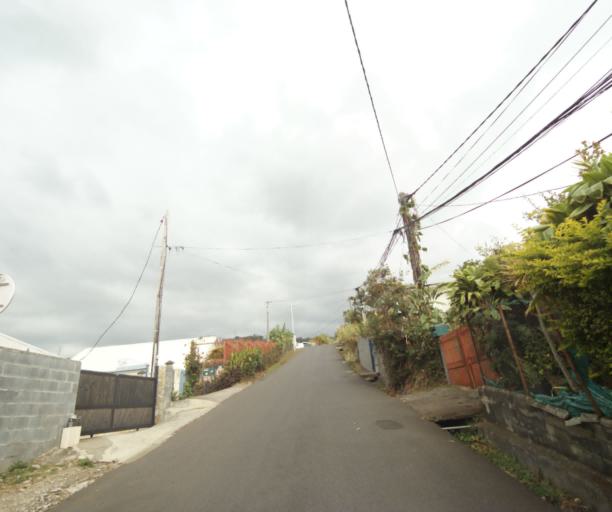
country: RE
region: Reunion
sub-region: Reunion
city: Saint-Paul
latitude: -21.0300
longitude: 55.3101
